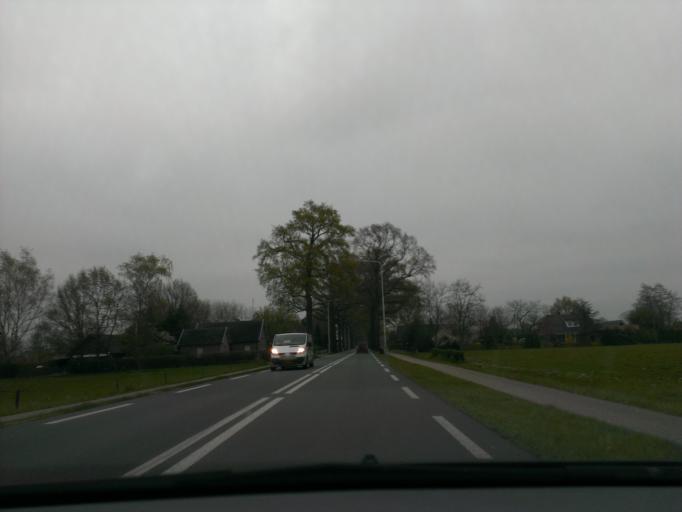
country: NL
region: Gelderland
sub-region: Gemeente Apeldoorn
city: Apeldoorn
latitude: 52.2307
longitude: 6.0240
